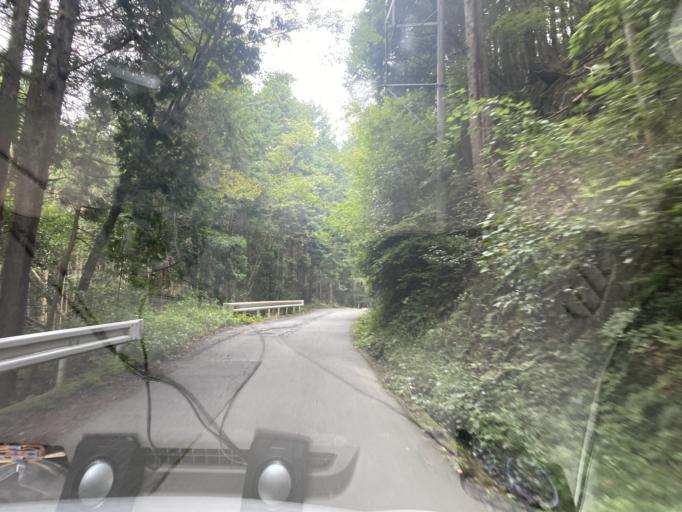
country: JP
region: Nara
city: Nara-shi
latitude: 34.6841
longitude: 135.8971
